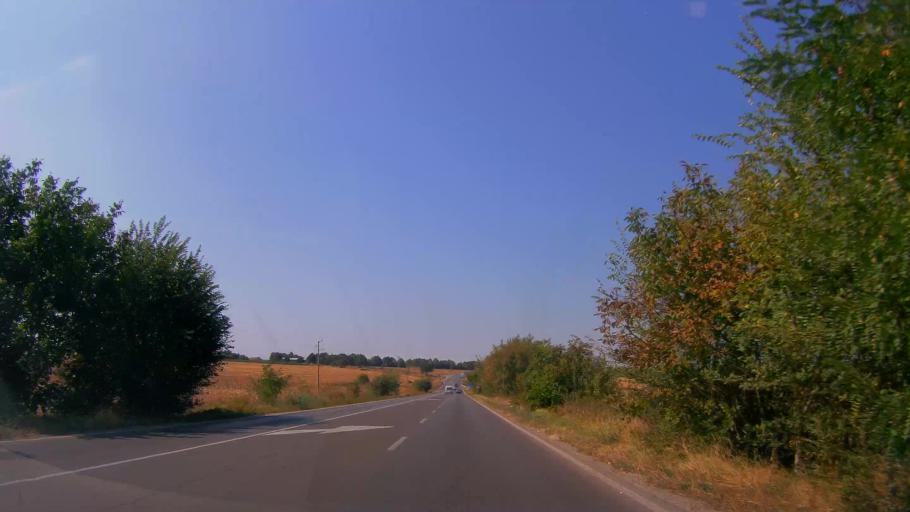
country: BG
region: Ruse
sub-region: Obshtina Vetovo
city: Senovo
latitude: 43.5666
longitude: 26.3292
